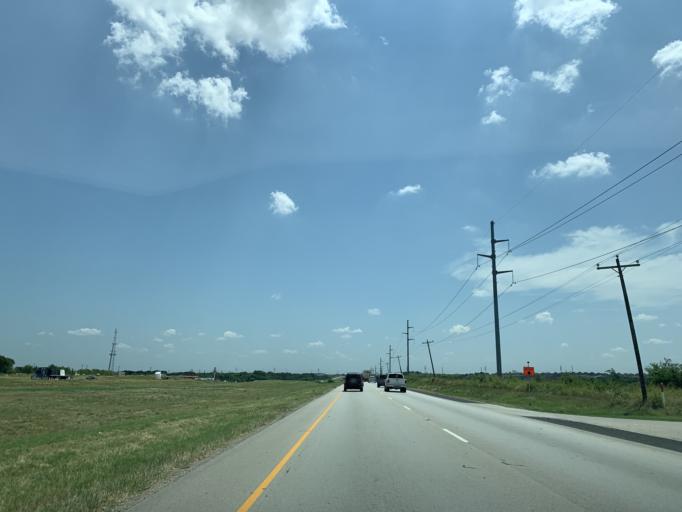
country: US
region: Texas
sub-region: Denton County
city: Roanoke
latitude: 33.0252
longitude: -97.2634
